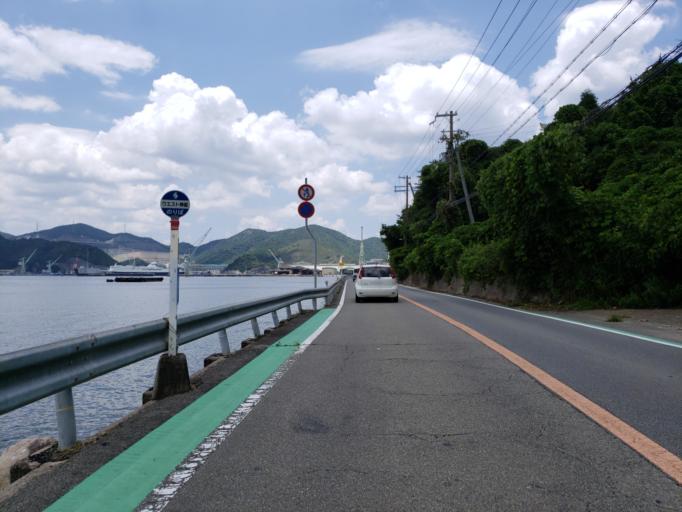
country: JP
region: Hyogo
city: Aioi
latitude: 34.7878
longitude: 134.4750
